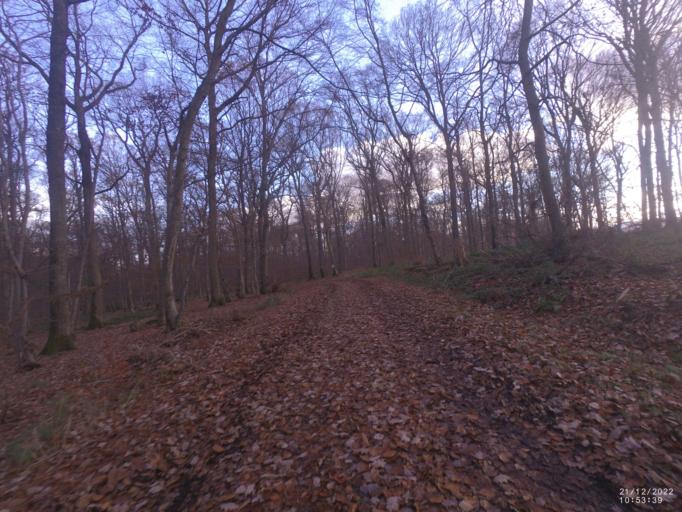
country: DE
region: Rheinland-Pfalz
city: Konigsfeld
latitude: 50.4972
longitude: 7.1939
